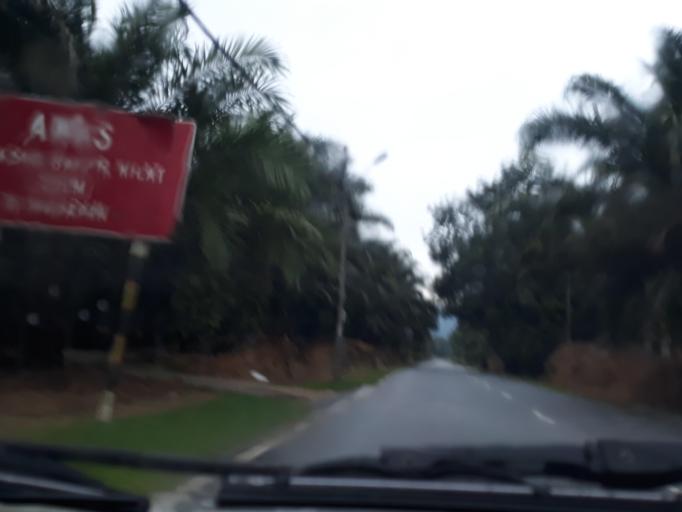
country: MY
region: Kedah
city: Kulim
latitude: 5.2342
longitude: 100.6035
